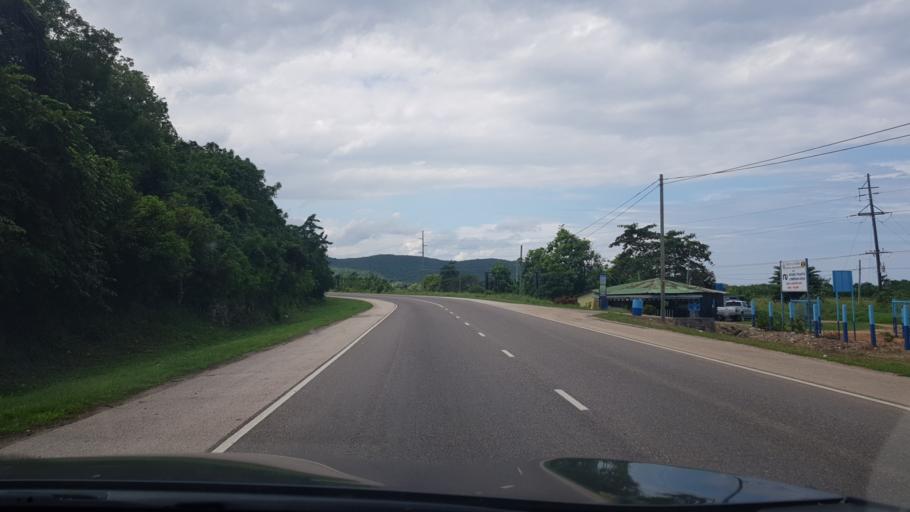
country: JM
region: Trelawny
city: Duncans
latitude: 18.4766
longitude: -77.4857
